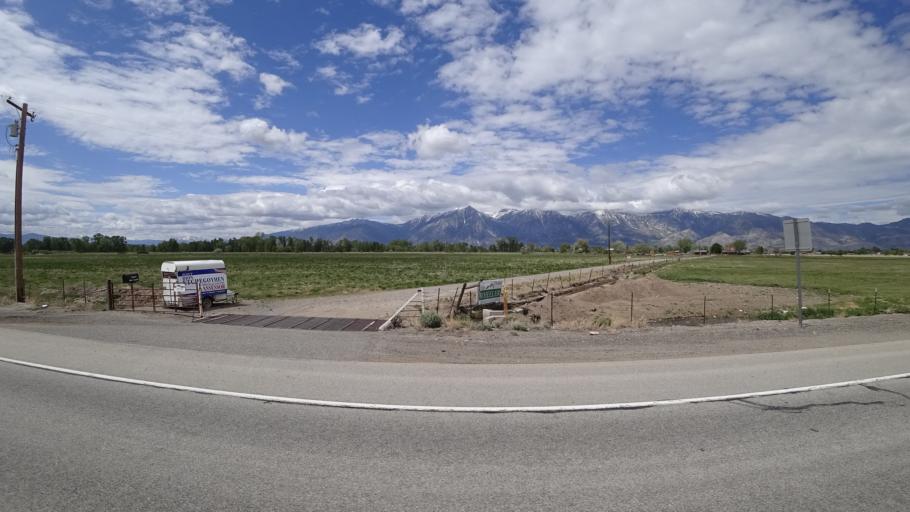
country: US
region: Nevada
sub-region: Douglas County
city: Gardnerville
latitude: 38.9288
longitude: -119.7307
